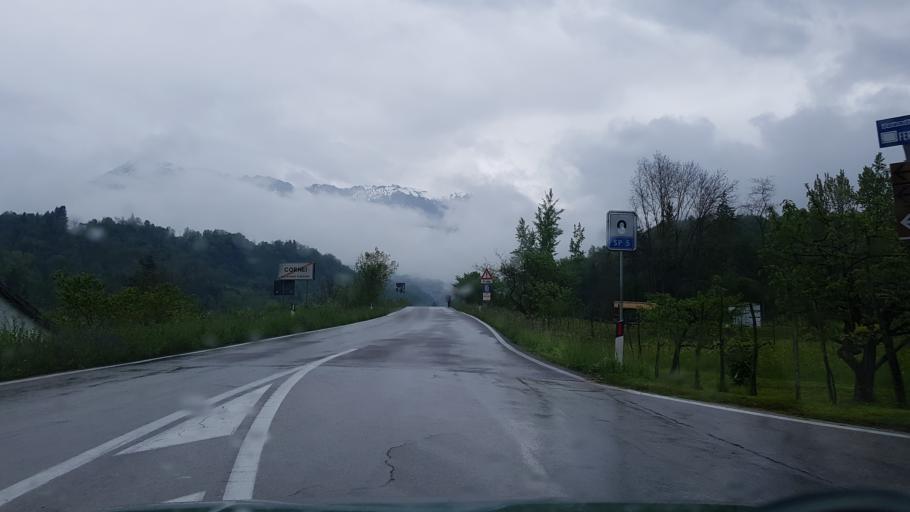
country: IT
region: Veneto
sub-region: Provincia di Belluno
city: Puos d'Alpago
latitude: 46.1479
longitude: 12.3840
